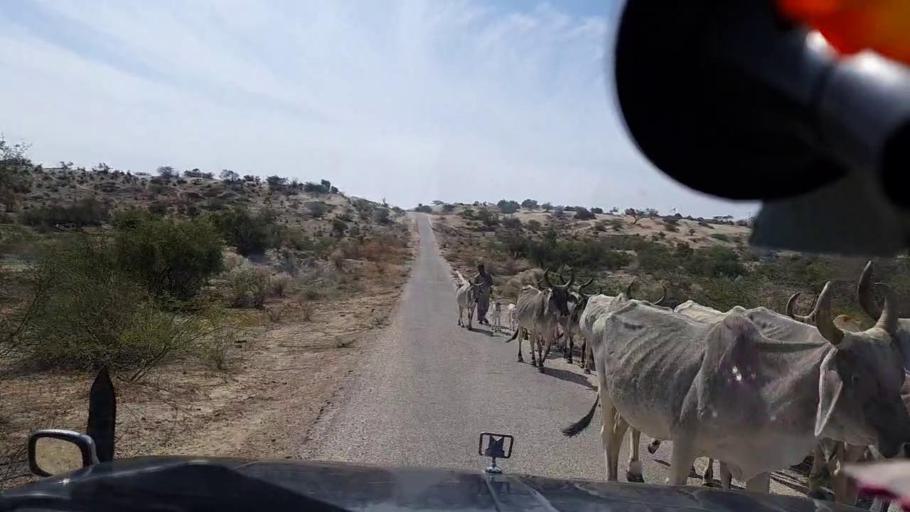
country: PK
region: Sindh
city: Diplo
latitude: 24.4019
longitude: 69.5883
